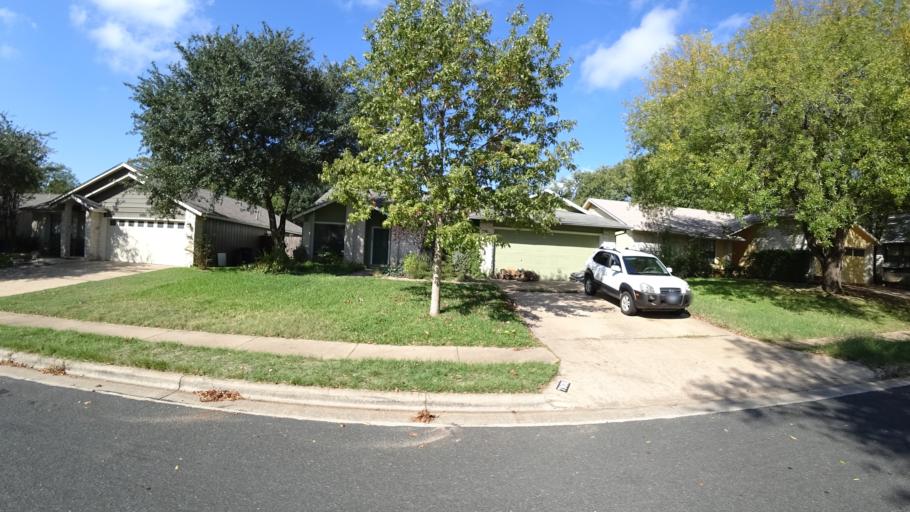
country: US
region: Texas
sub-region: Travis County
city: Shady Hollow
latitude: 30.1972
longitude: -97.8227
